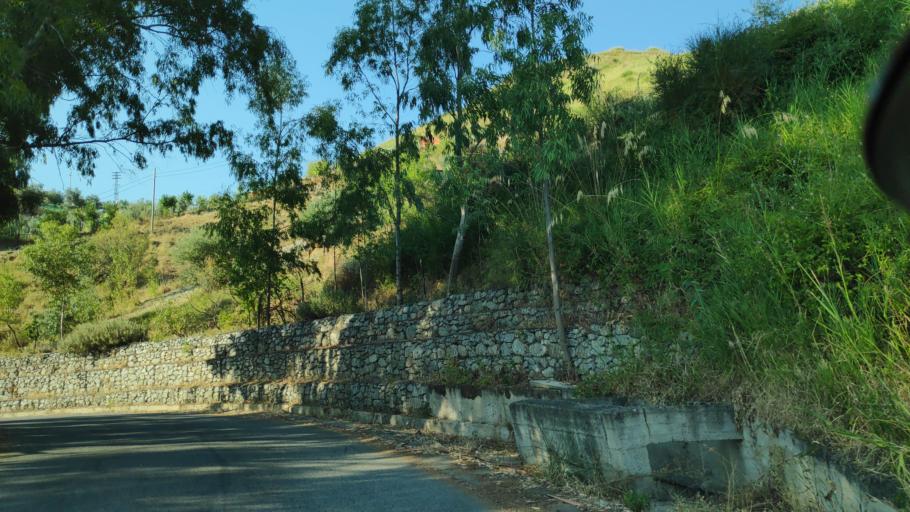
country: IT
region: Calabria
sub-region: Provincia di Catanzaro
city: Guardavalle
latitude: 38.5067
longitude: 16.5081
